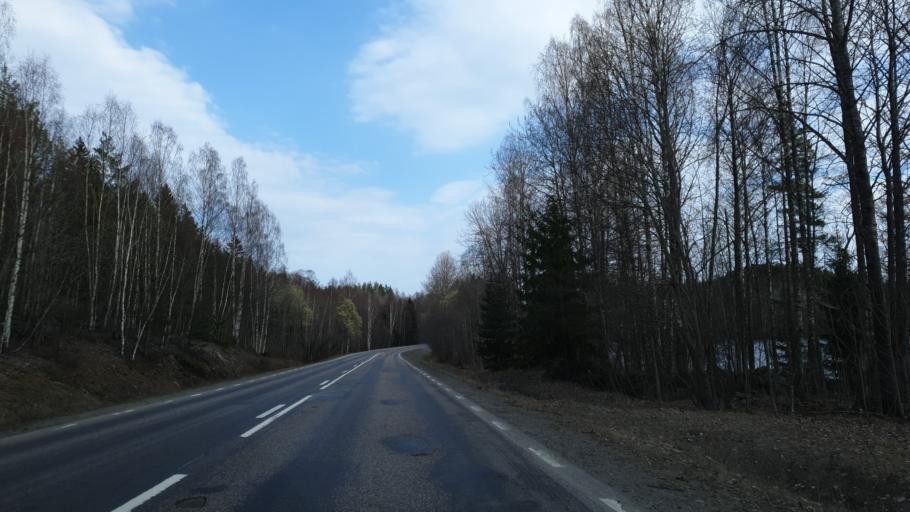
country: SE
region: Gaevleborg
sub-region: Hudiksvalls Kommun
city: Iggesund
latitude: 61.6491
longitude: 17.0418
